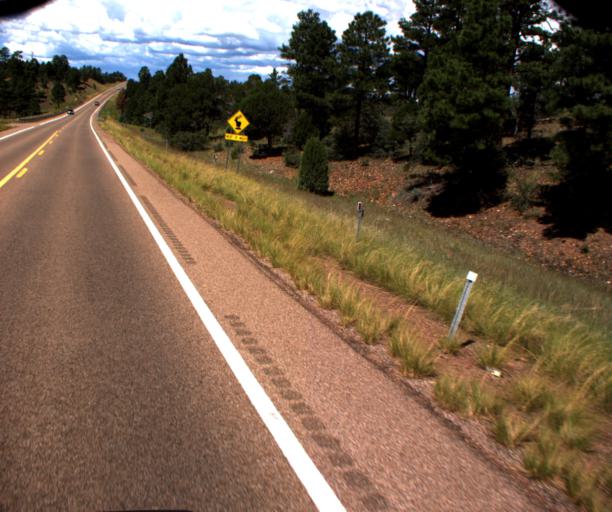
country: US
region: Arizona
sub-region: Navajo County
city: Heber-Overgaard
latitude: 34.3676
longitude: -110.3838
